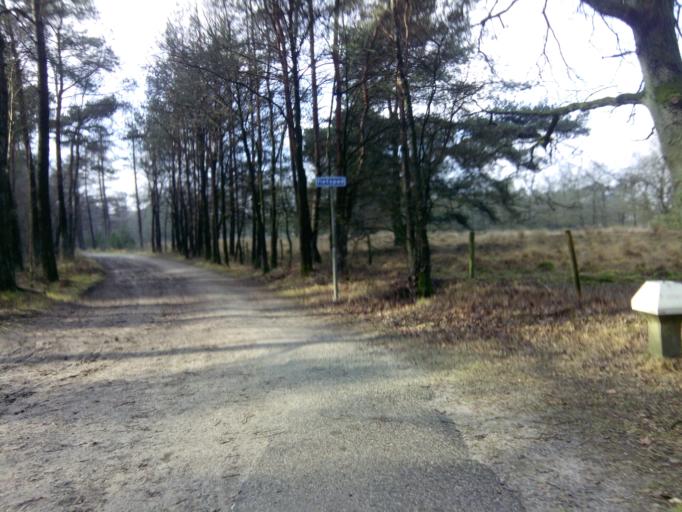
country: NL
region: Utrecht
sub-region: Gemeente Utrechtse Heuvelrug
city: Leersum
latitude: 52.0332
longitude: 5.4347
